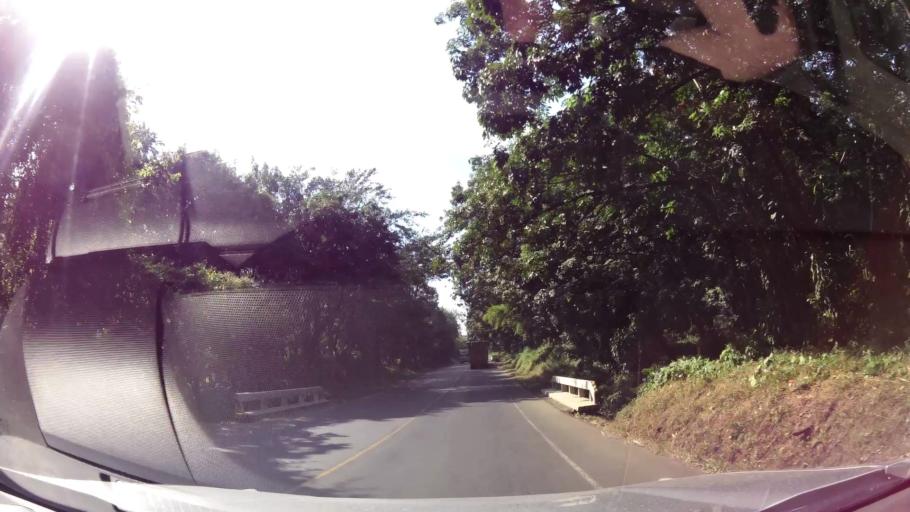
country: GT
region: Retalhuleu
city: San Sebastian
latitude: 14.5512
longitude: -91.6328
